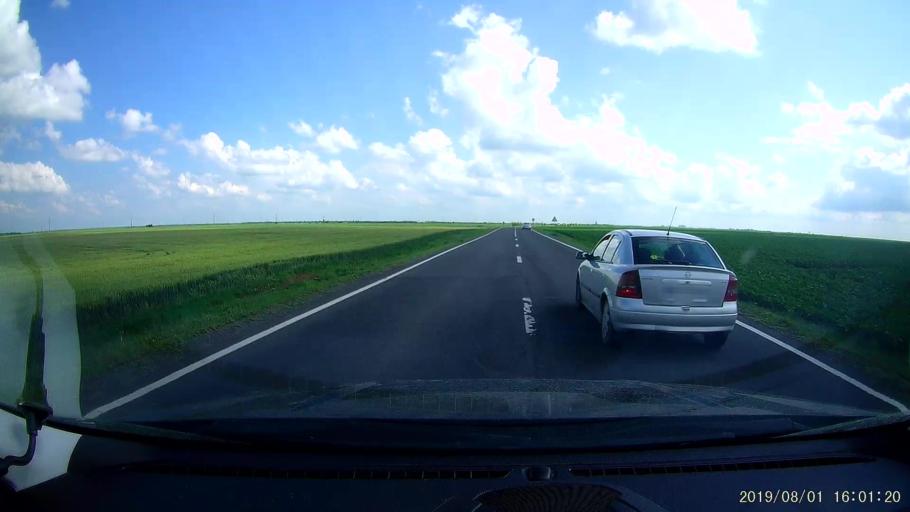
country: RO
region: Ialomita
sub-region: Comuna Ciulnita
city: Ciulnita
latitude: 44.5104
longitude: 27.3902
